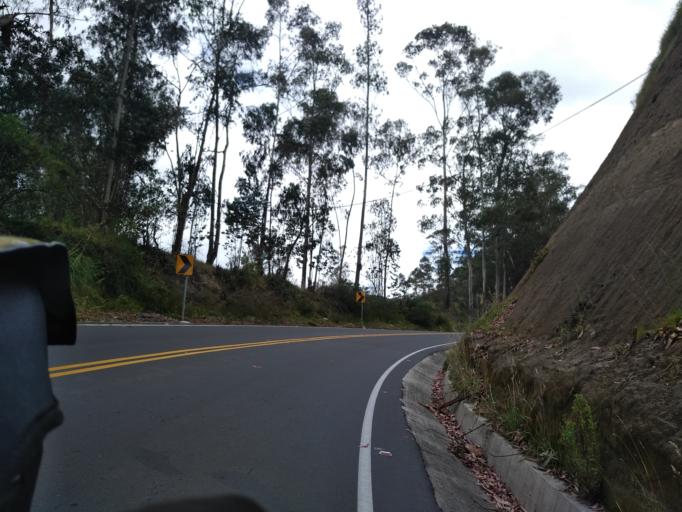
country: EC
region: Cotopaxi
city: Saquisili
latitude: -0.7207
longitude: -78.8887
